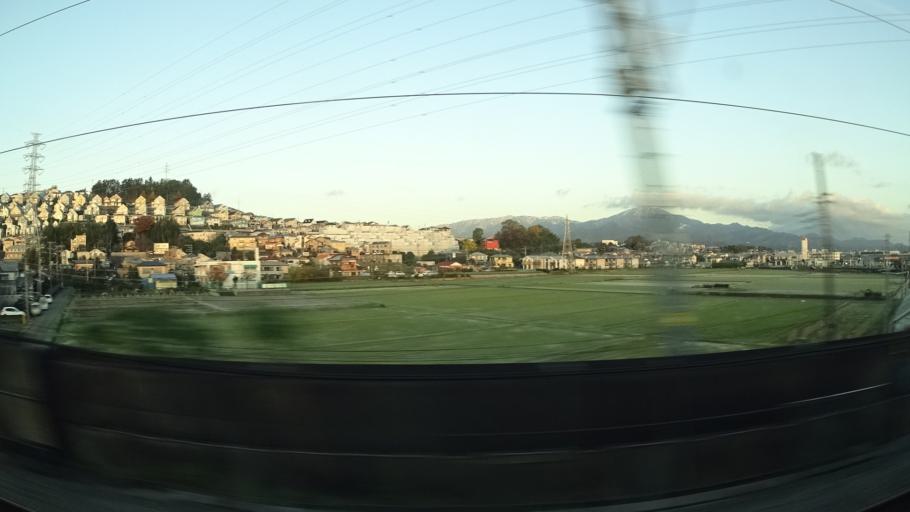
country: JP
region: Kanagawa
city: Oiso
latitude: 35.3413
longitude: 139.3065
